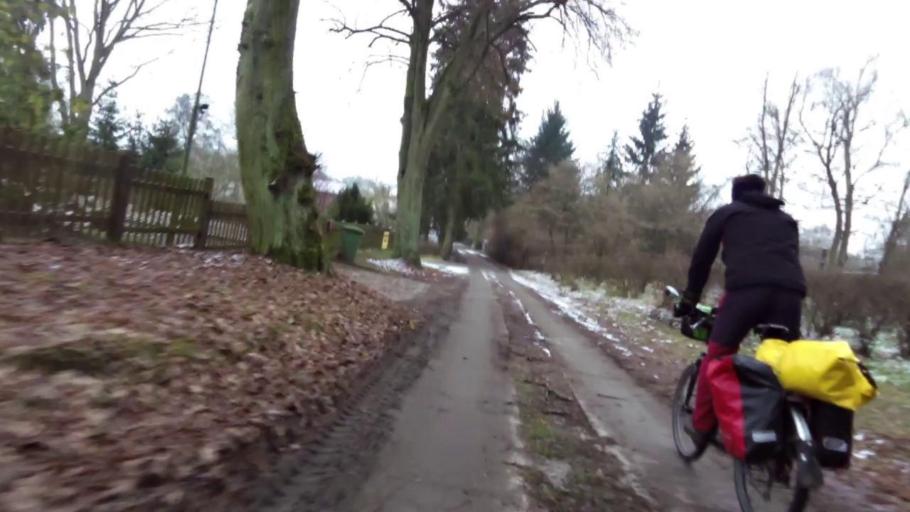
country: PL
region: West Pomeranian Voivodeship
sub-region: Powiat walecki
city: Walcz
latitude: 53.3026
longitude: 16.4752
